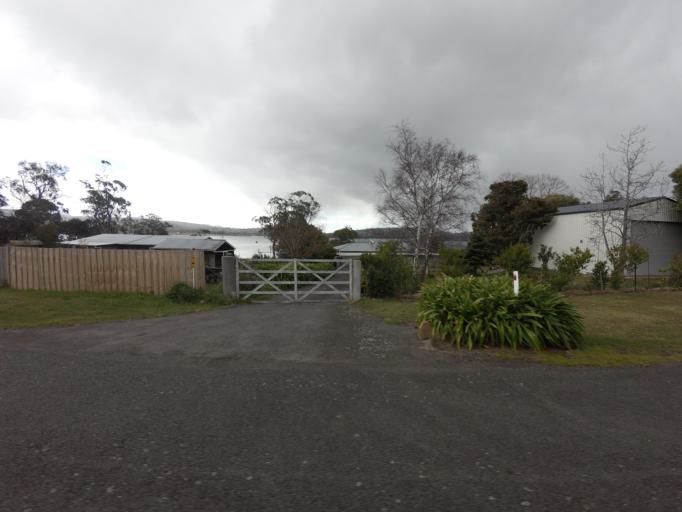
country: AU
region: Tasmania
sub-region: Sorell
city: Sorell
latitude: -42.5292
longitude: 147.9049
